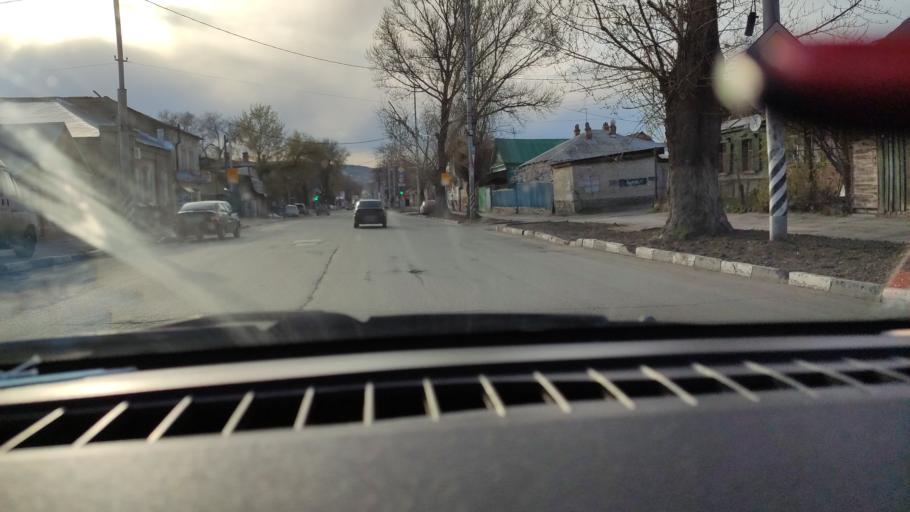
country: RU
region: Saratov
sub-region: Saratovskiy Rayon
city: Saratov
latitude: 51.5435
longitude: 46.0359
